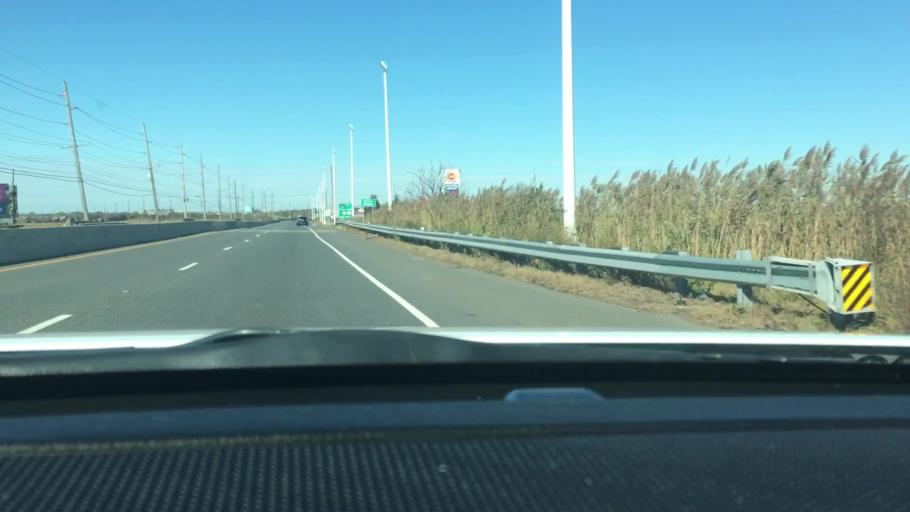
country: US
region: New Jersey
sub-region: Atlantic County
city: Absecon
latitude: 39.3921
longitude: -74.4858
